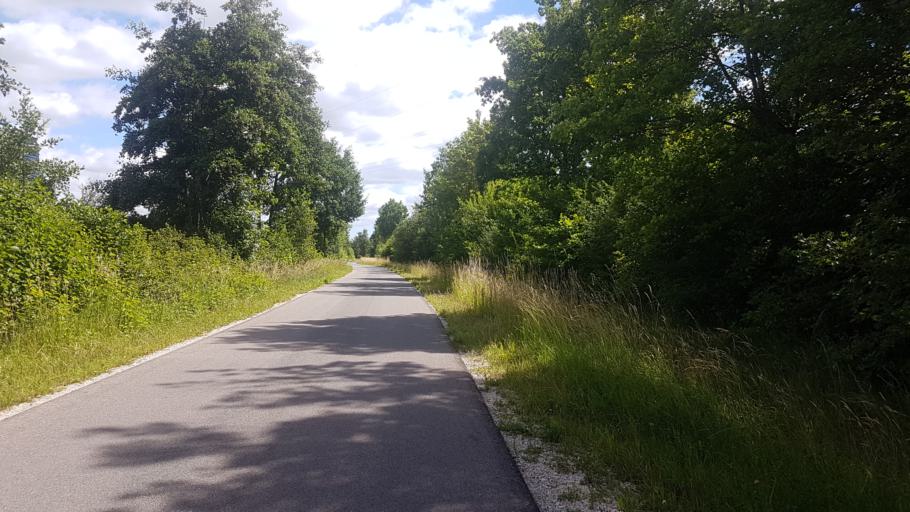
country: DE
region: Bavaria
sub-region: Regierungsbezirk Mittelfranken
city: Gunzenhausen
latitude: 49.1248
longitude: 10.7532
